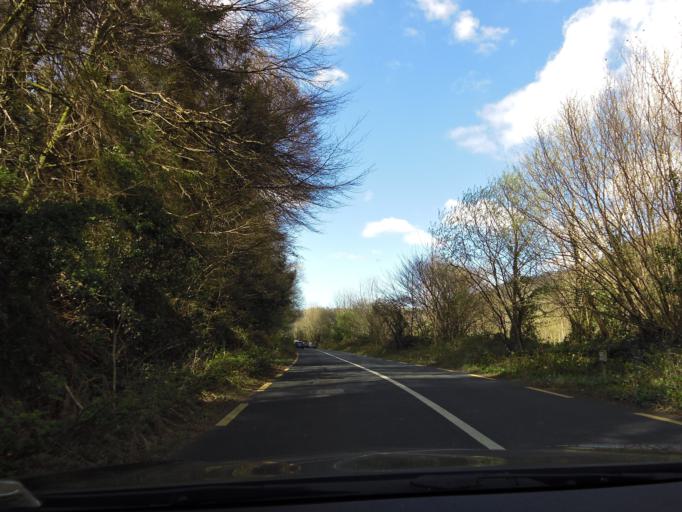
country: IE
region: Leinster
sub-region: Wicklow
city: Arklow
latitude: 52.8247
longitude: -6.2161
